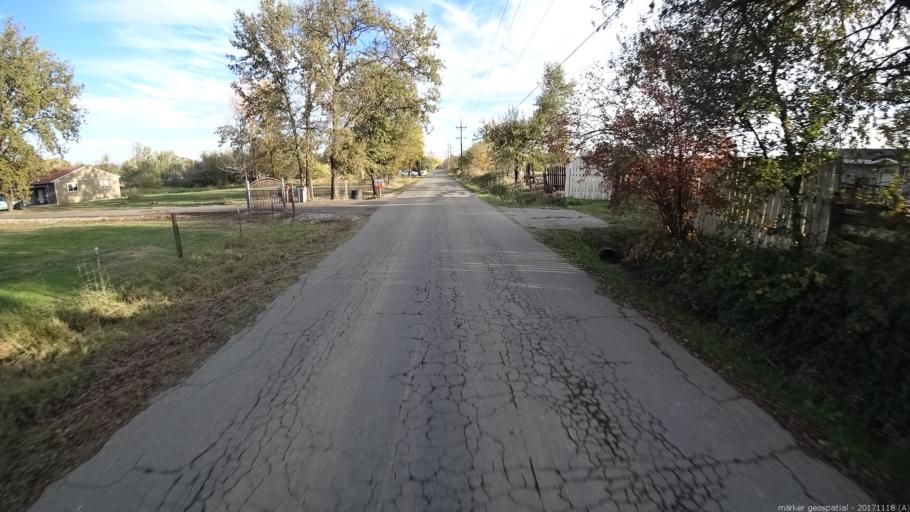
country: US
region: California
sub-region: Shasta County
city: Anderson
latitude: 40.4576
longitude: -122.3225
